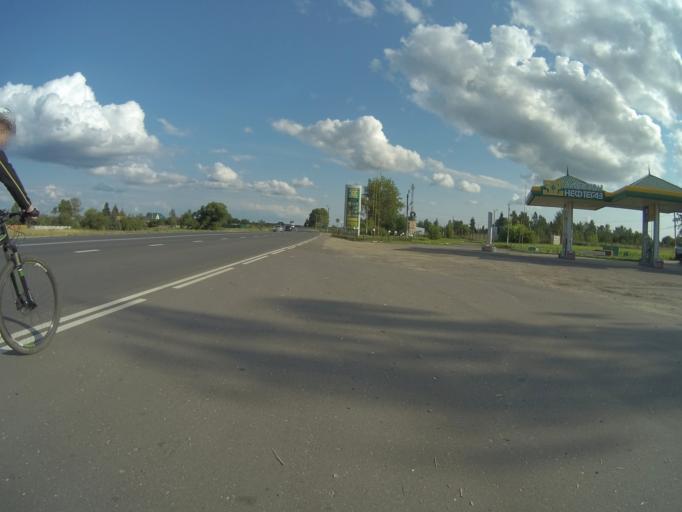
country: RU
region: Vladimir
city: Kideksha
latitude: 56.5542
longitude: 40.5479
